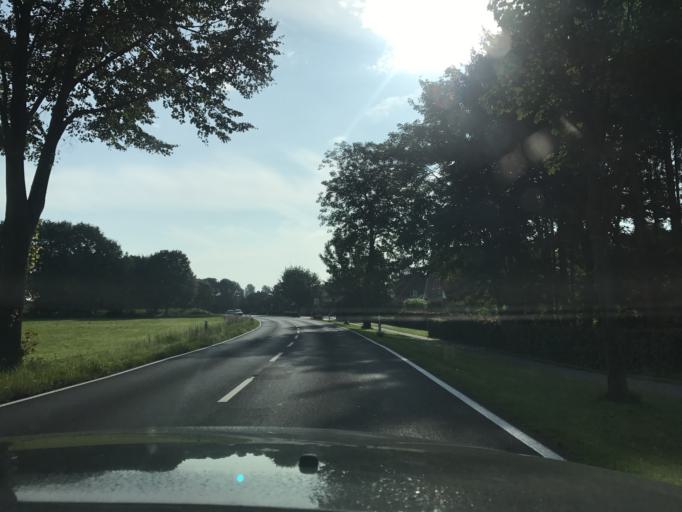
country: DE
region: Lower Saxony
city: Haselunne
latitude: 52.6580
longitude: 7.4250
